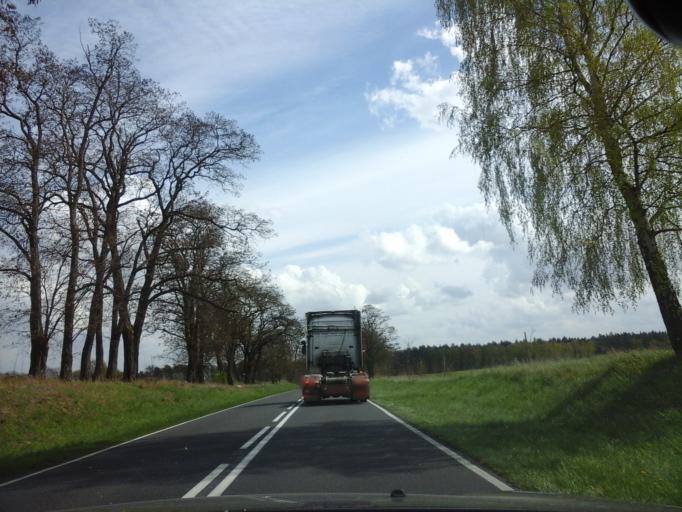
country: PL
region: West Pomeranian Voivodeship
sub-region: Powiat stargardzki
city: Suchan
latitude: 53.2018
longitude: 15.3376
